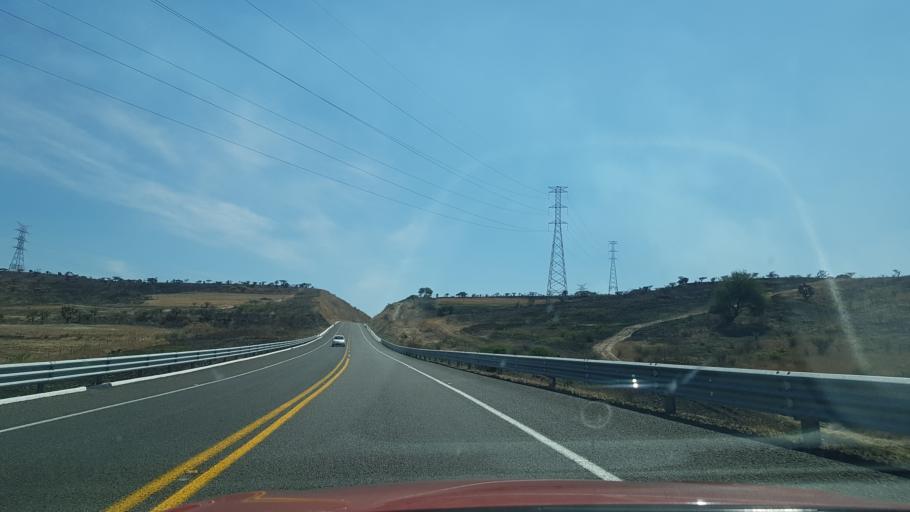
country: MX
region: Michoacan
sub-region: Tarimbaro
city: Uruetaro
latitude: 19.7659
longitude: -101.0743
